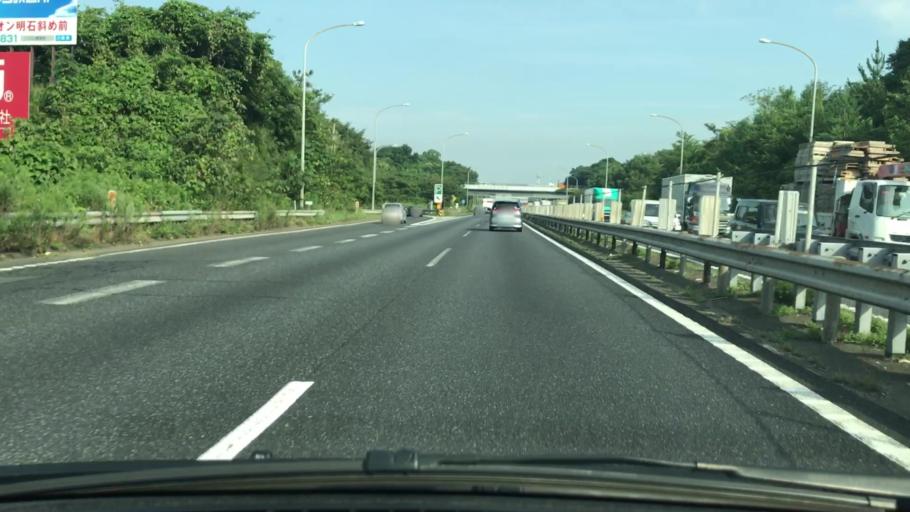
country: JP
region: Hyogo
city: Akashi
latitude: 34.7028
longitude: 134.9587
